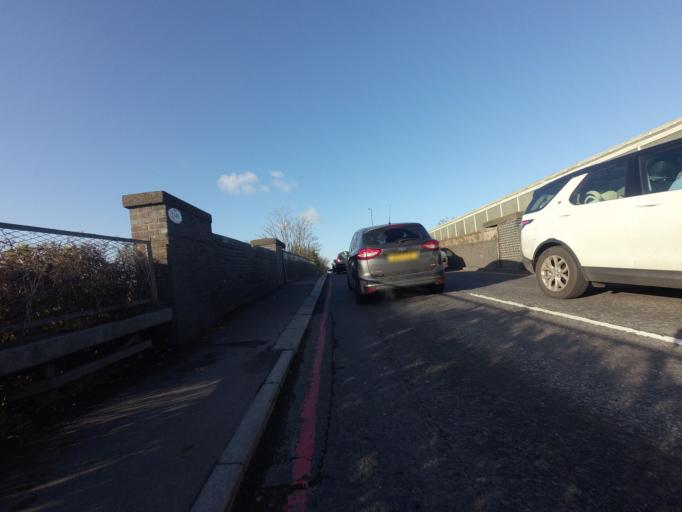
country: GB
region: England
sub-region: Greater London
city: Feltham
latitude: 51.4491
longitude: -0.4032
